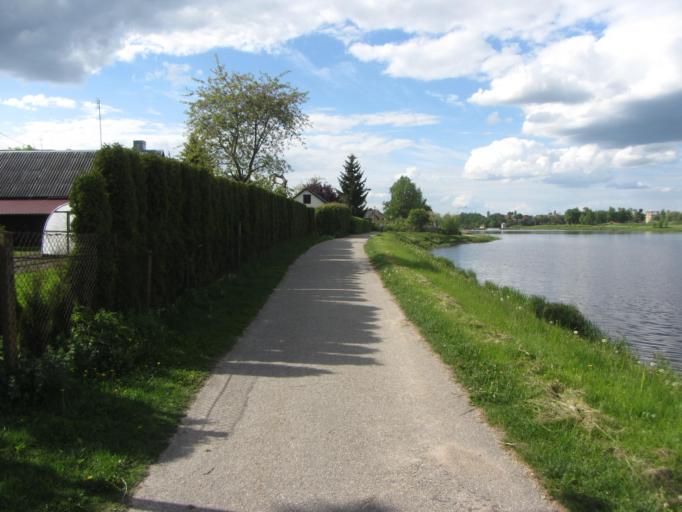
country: LT
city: Sirvintos
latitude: 55.0407
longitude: 24.9591
